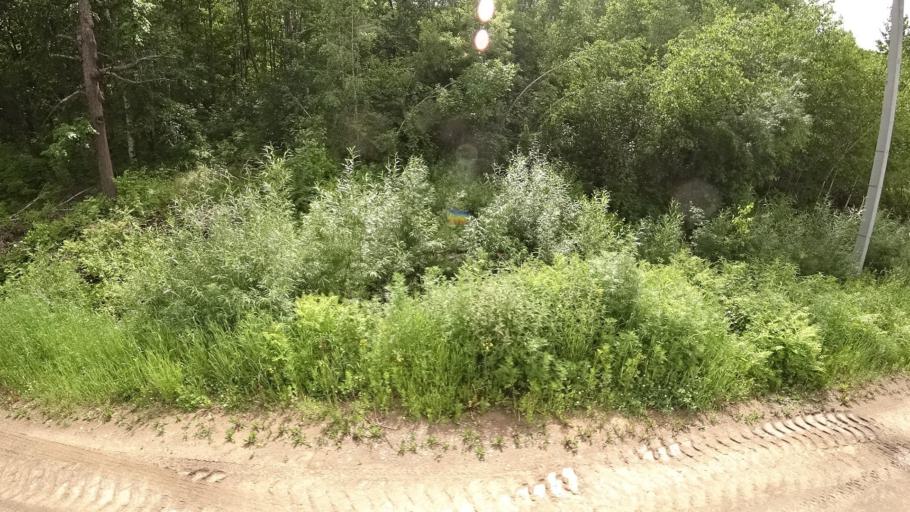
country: RU
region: Khabarovsk Krai
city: Litovko
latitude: 49.3669
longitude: 135.1819
